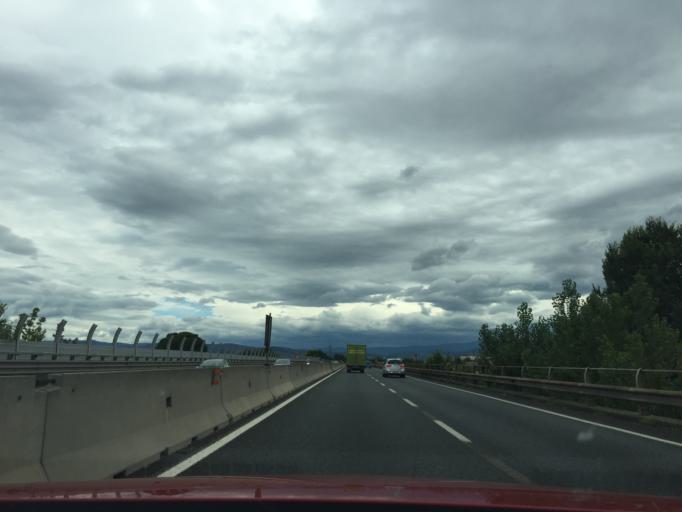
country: IT
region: Tuscany
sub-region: Province of Florence
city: San Donnino
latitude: 43.7736
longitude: 11.1378
